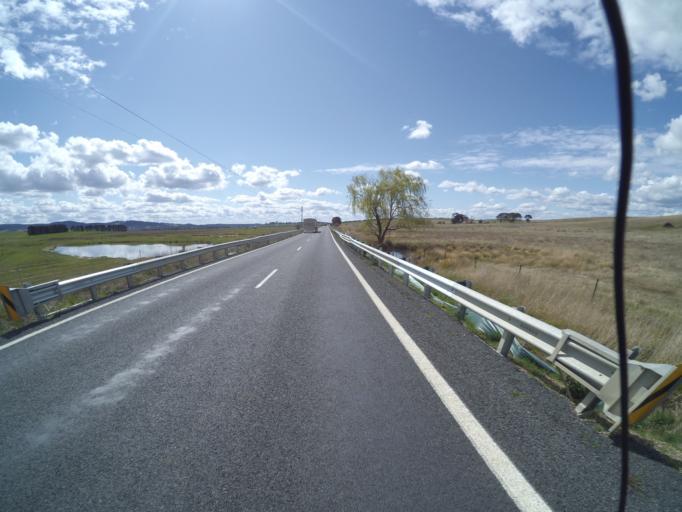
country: AU
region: New South Wales
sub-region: Goulburn Mulwaree
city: Goulburn
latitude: -34.8585
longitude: 149.6838
